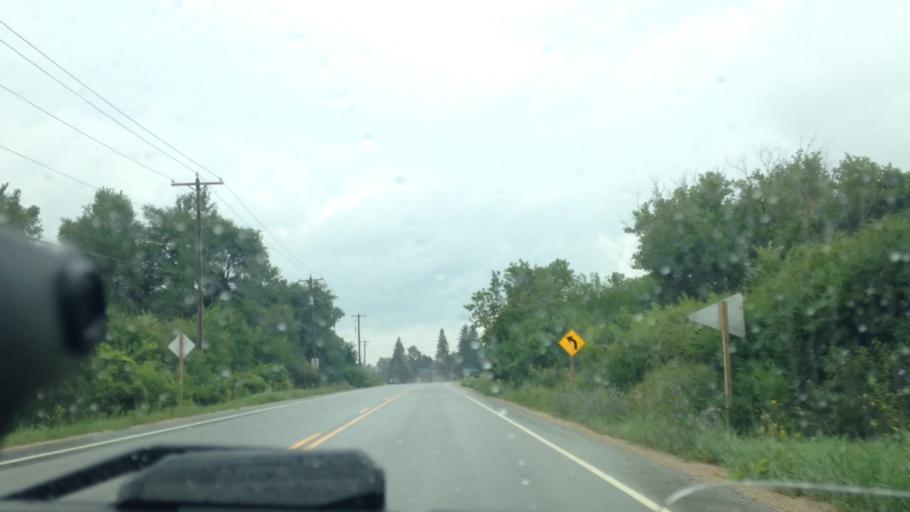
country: US
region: Wisconsin
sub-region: Washington County
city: Richfield
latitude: 43.2308
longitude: -88.1836
